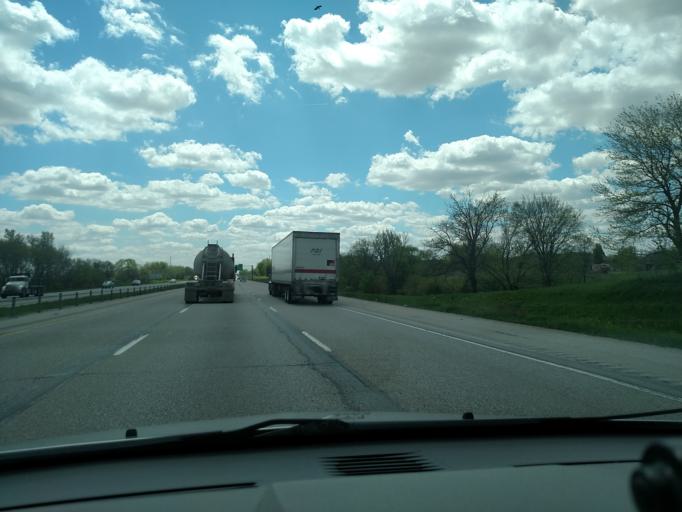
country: US
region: Iowa
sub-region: Polk County
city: Ankeny
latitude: 41.7230
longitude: -93.5767
